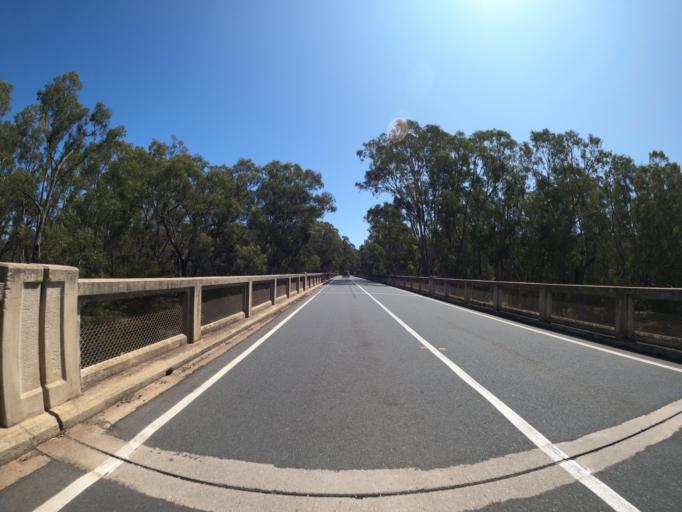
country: AU
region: New South Wales
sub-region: Corowa Shire
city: Corowa
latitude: -36.0686
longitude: 146.2003
